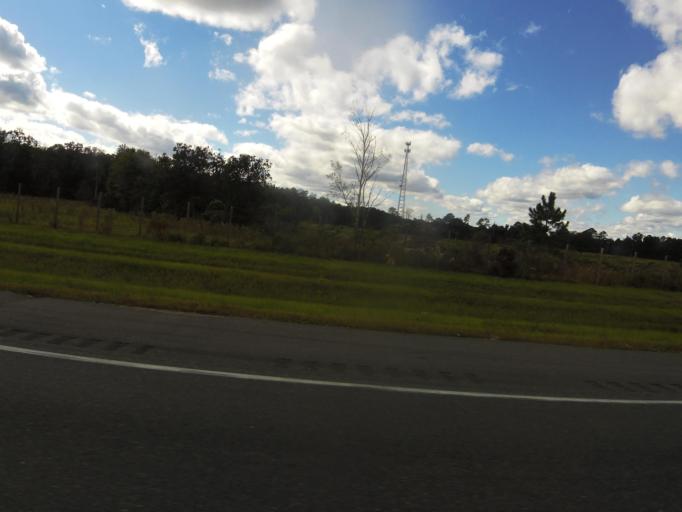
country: US
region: Florida
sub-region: Bradford County
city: Starke
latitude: 29.9172
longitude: -82.1350
